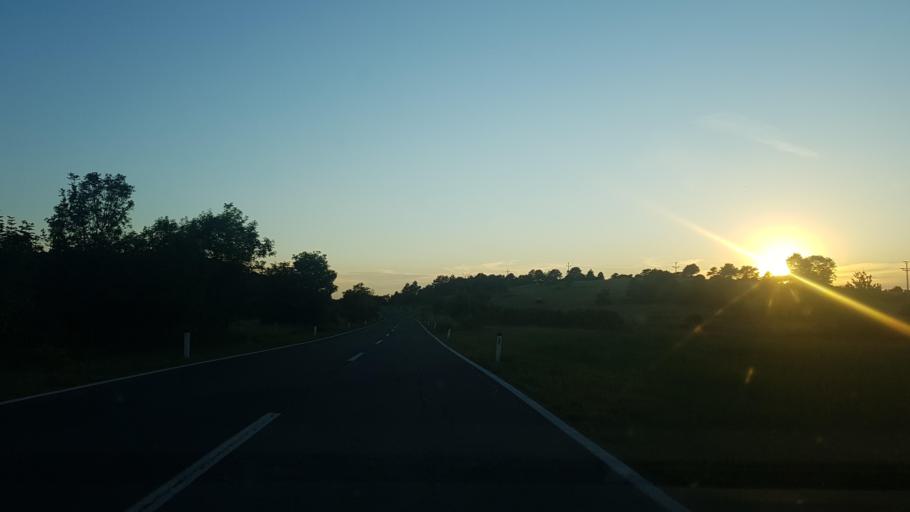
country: SI
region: Divaca
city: Divaca
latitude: 45.7185
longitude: 14.0217
